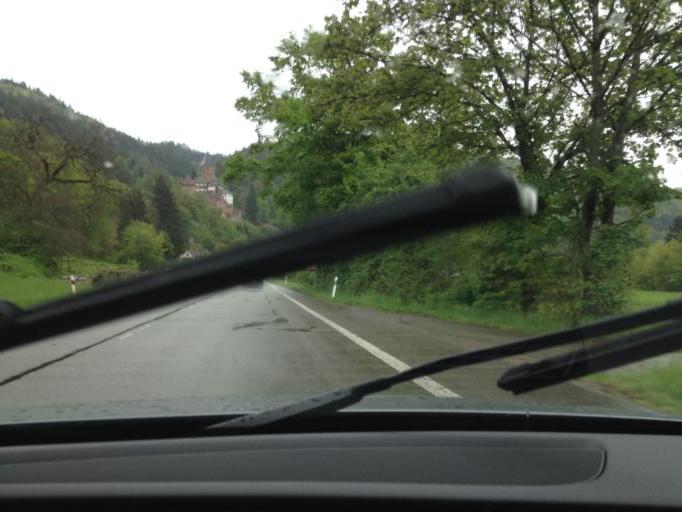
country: DE
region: Baden-Wuerttemberg
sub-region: Karlsruhe Region
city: Zwingenberg
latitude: 49.4193
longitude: 9.0267
